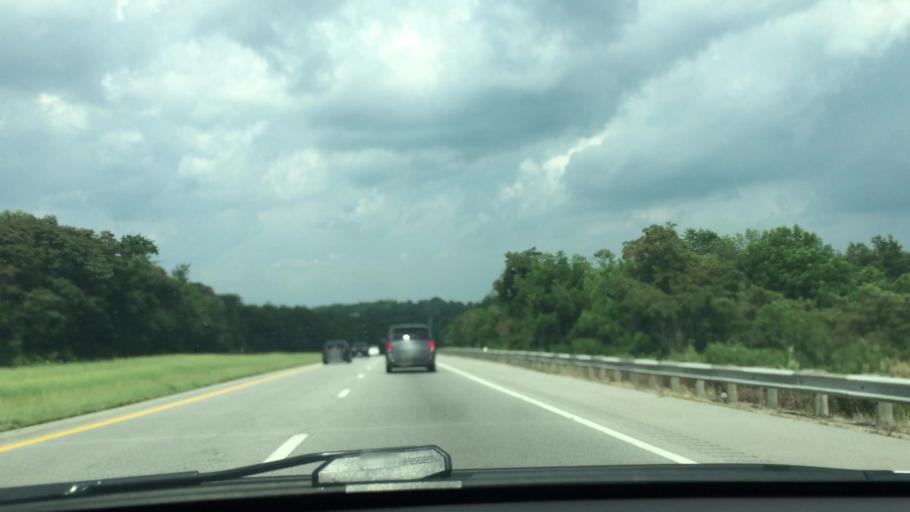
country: US
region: Ohio
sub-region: Belmont County
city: Barnesville
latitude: 40.0563
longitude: -81.2638
